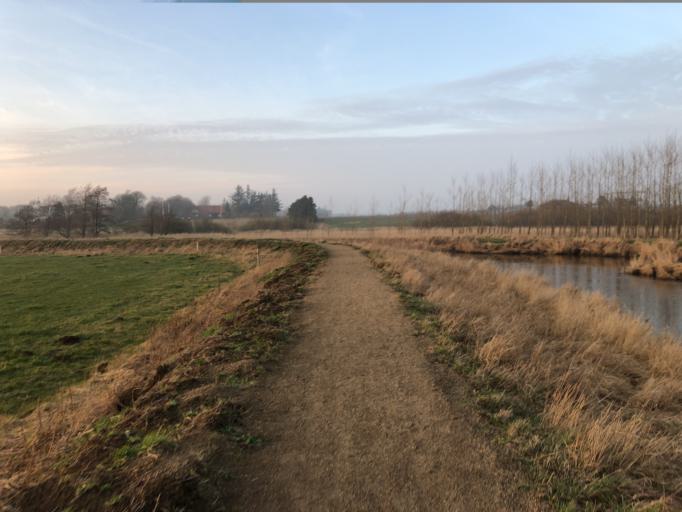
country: DK
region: Central Jutland
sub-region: Holstebro Kommune
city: Ulfborg
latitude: 56.3417
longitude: 8.3565
